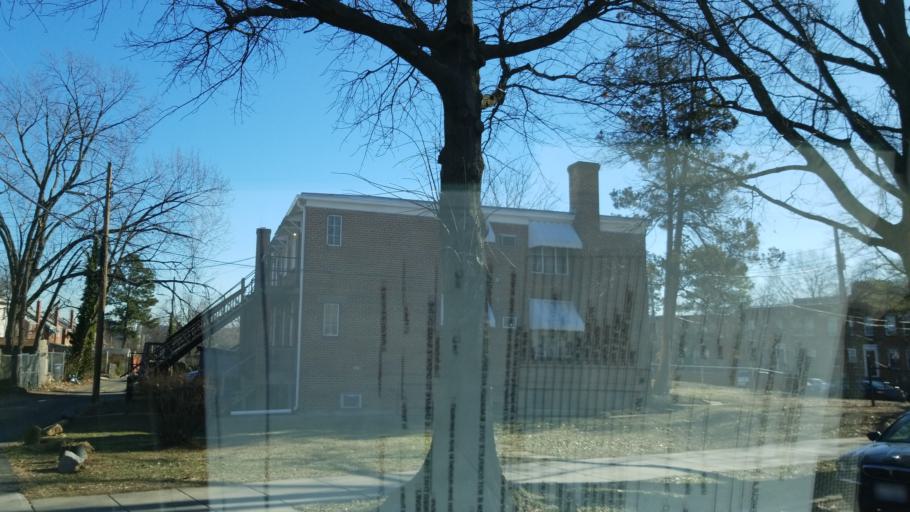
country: US
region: Maryland
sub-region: Prince George's County
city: Glassmanor
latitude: 38.8248
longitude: -77.0124
